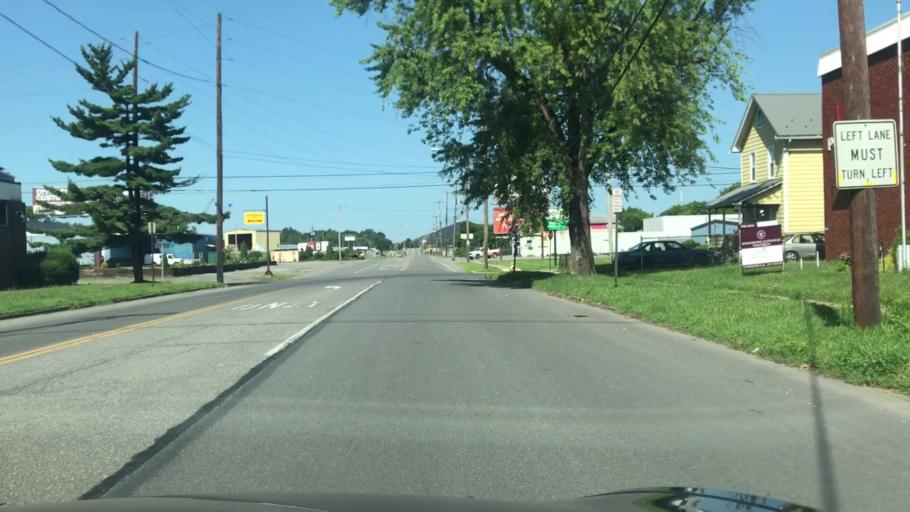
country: US
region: Pennsylvania
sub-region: Lycoming County
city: Duboistown
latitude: 41.2373
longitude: -77.0316
